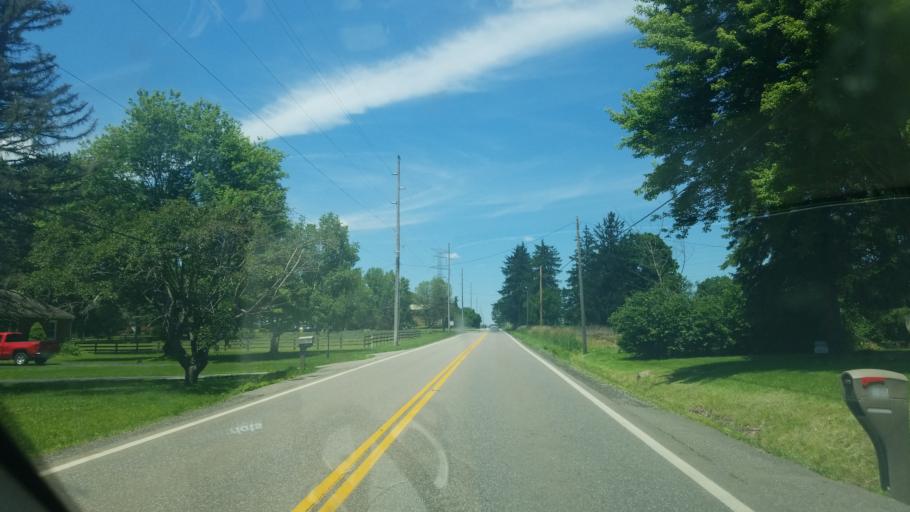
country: US
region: Ohio
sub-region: Columbiana County
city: Lisbon
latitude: 40.8090
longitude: -80.7909
